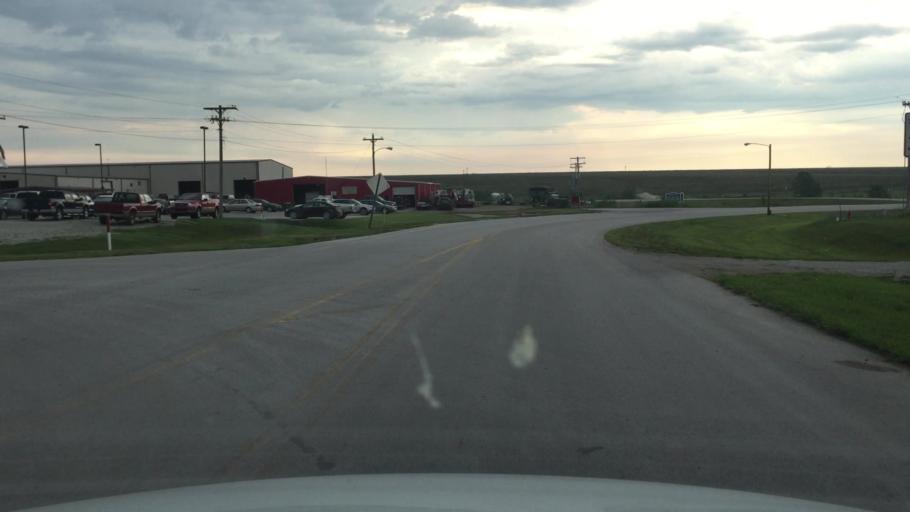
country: US
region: Kansas
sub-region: Nemaha County
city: Sabetha
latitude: 39.9033
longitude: -95.7874
